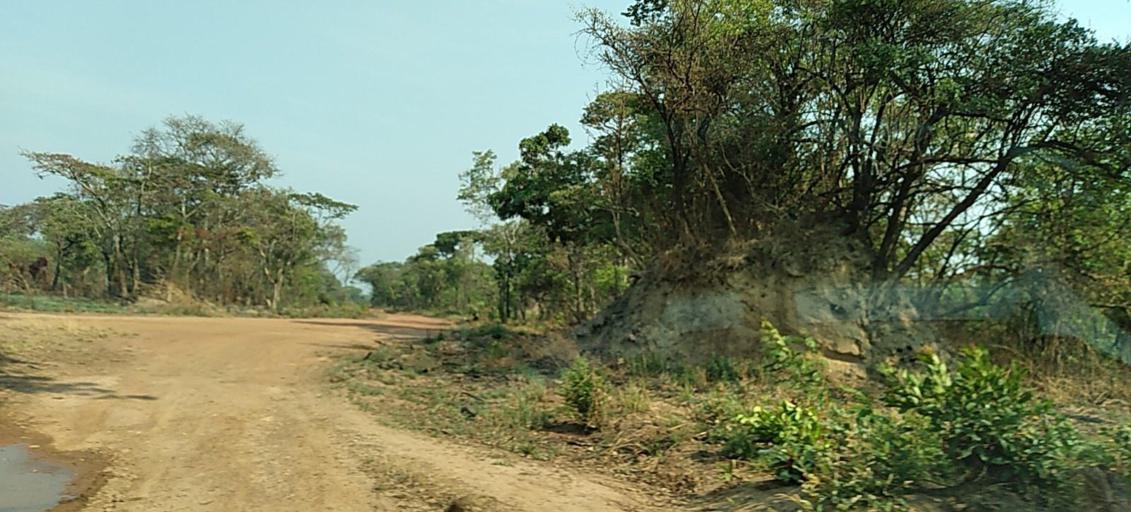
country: ZM
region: North-Western
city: Kansanshi
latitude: -12.2673
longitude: 26.9511
